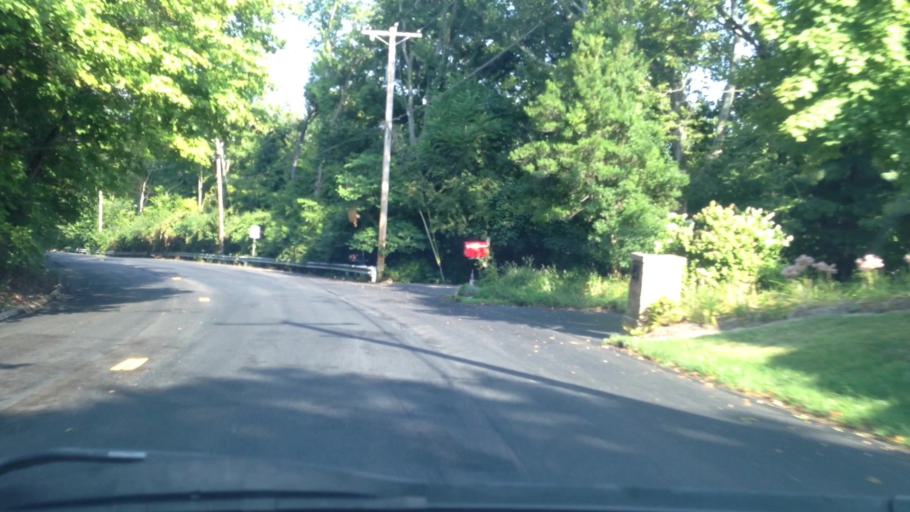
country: US
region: Missouri
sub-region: Saint Louis County
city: Des Peres
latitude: 38.5786
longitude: -90.4357
